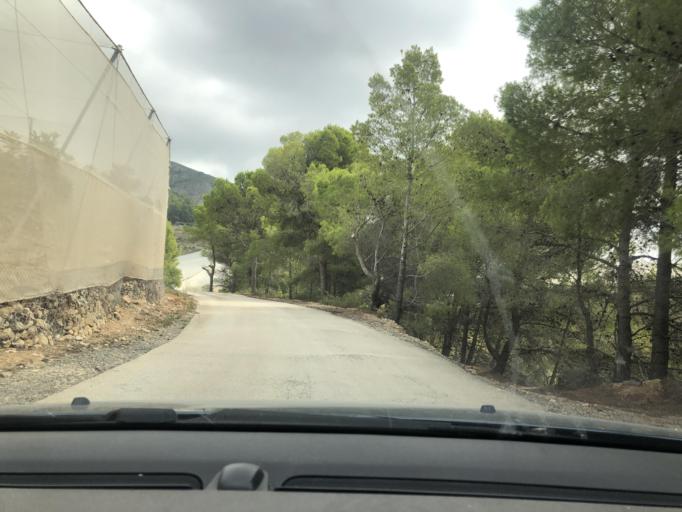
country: ES
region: Valencia
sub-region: Provincia de Alicante
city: Callosa d'En Sarria
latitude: 38.6540
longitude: -0.0920
